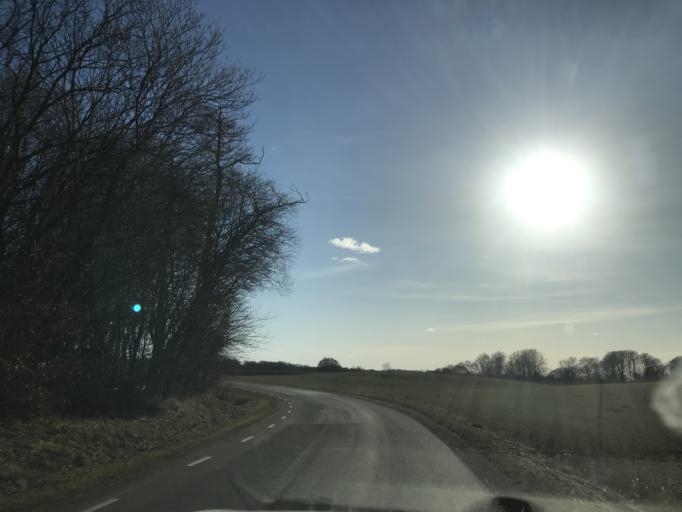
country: SE
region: Skane
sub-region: Ystads Kommun
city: Ystad
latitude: 55.5490
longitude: 13.8048
